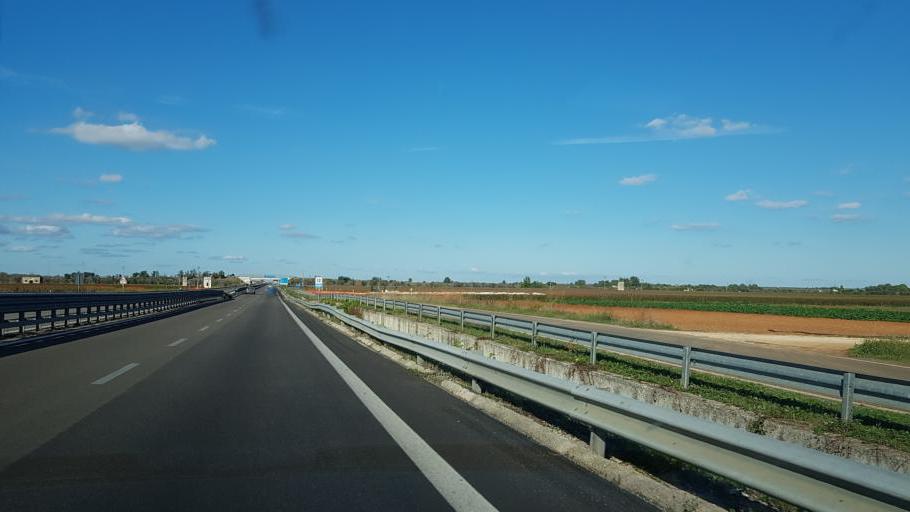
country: IT
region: Apulia
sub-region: Provincia di Lecce
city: Collemeto
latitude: 40.2512
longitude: 18.1159
